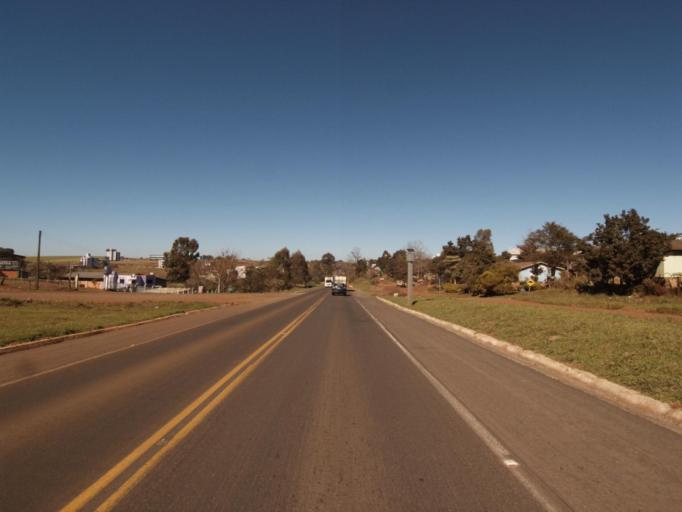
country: BR
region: Santa Catarina
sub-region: Chapeco
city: Chapeco
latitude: -26.8416
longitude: -52.9830
